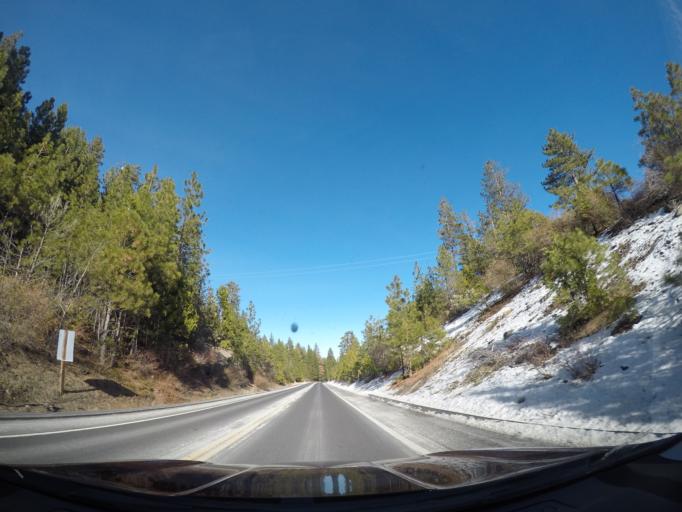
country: US
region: California
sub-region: Tuolumne County
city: Twain Harte
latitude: 38.0826
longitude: -120.1586
